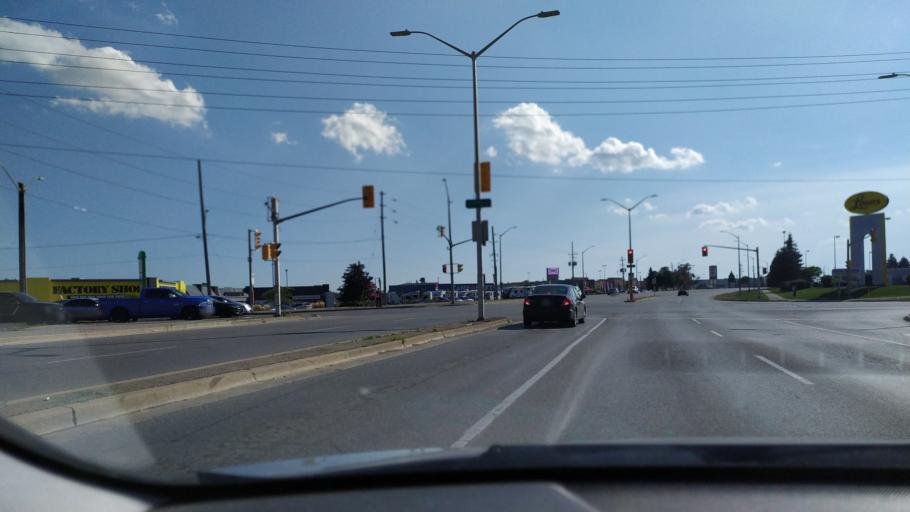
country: CA
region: Ontario
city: London
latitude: 42.9412
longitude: -81.2579
